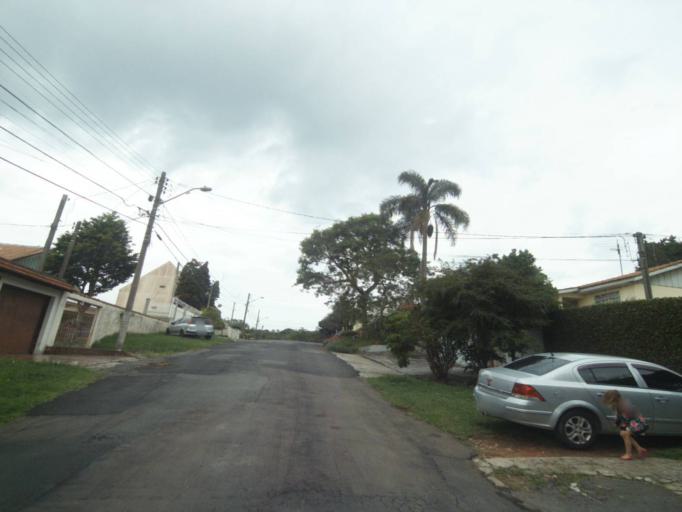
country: BR
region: Parana
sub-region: Curitiba
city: Curitiba
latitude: -25.3987
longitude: -49.2995
